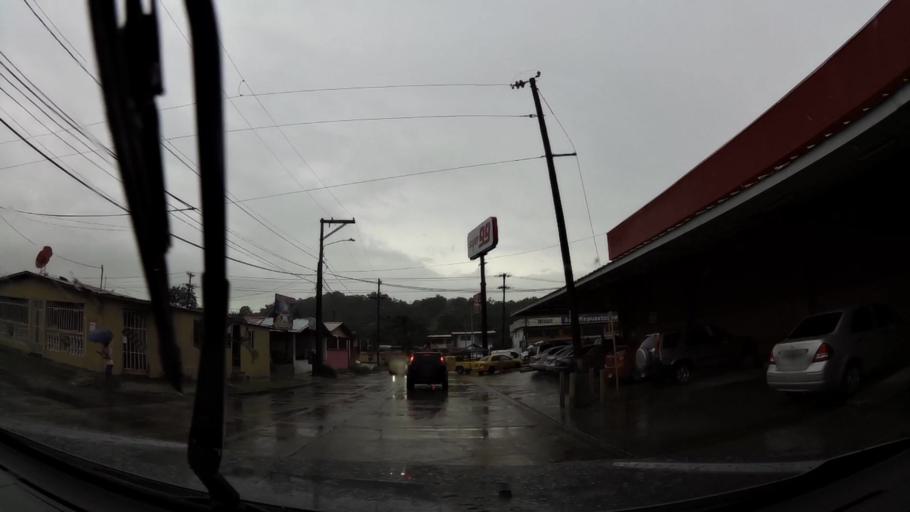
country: PA
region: Colon
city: Sabanitas
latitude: 9.3490
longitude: -79.8092
